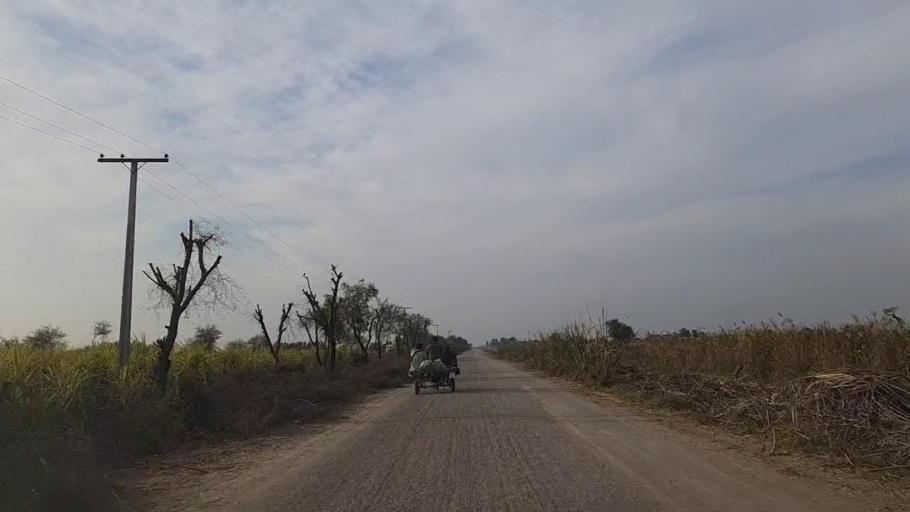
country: PK
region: Sindh
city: Daur
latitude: 26.4891
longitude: 68.4610
